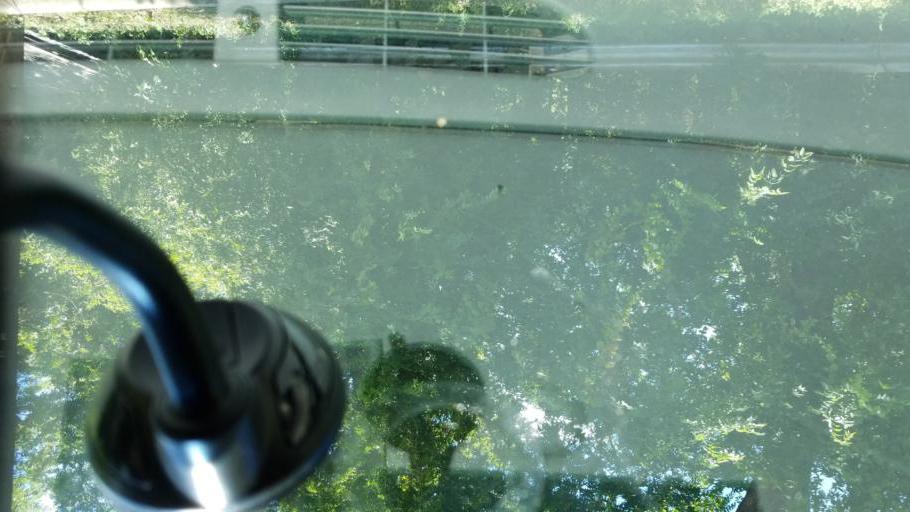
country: US
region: Texas
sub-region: Dallas County
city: Cockrell Hill
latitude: 32.6864
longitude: -96.8126
